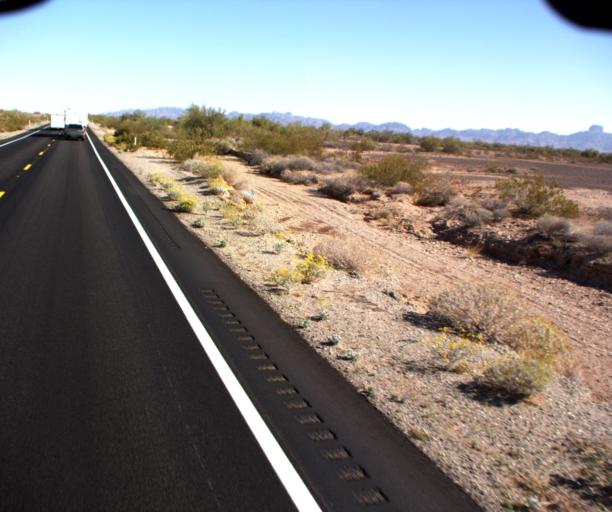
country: US
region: Arizona
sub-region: Yuma County
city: Wellton
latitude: 32.9972
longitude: -114.2864
